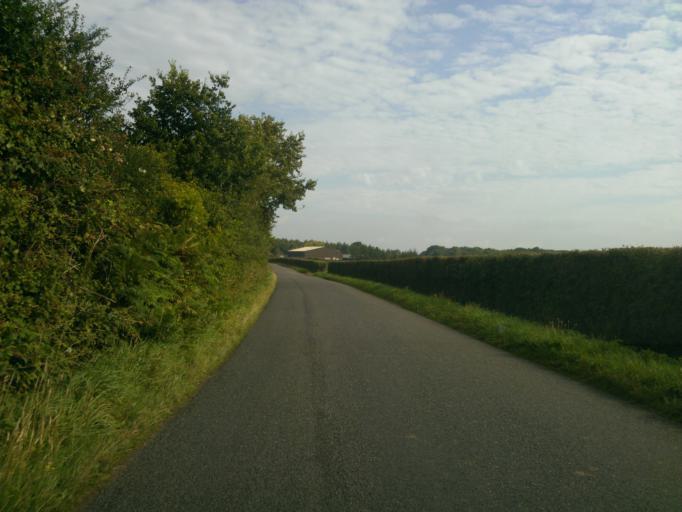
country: GB
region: England
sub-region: Essex
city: Saint Osyth
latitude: 51.8278
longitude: 1.1026
